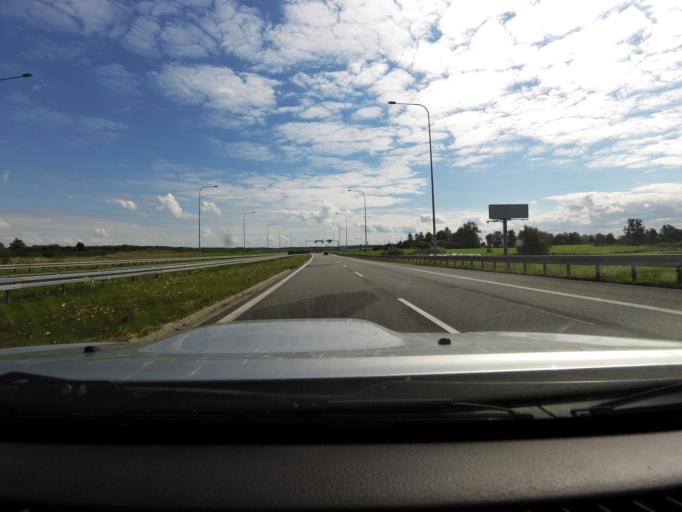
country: PL
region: Warmian-Masurian Voivodeship
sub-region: Powiat ostrodzki
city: Milomlyn
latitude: 53.7793
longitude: 19.8114
